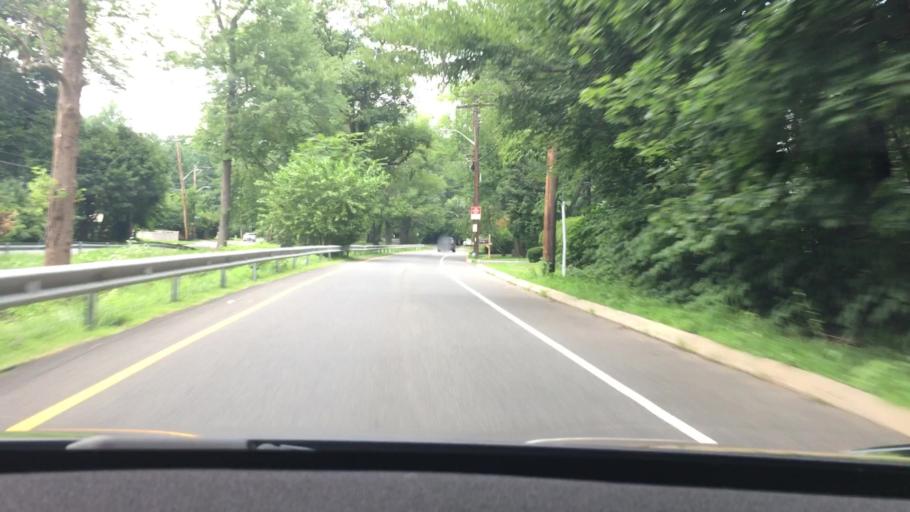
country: US
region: New York
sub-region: Westchester County
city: New Rochelle
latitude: 40.9406
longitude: -73.7785
